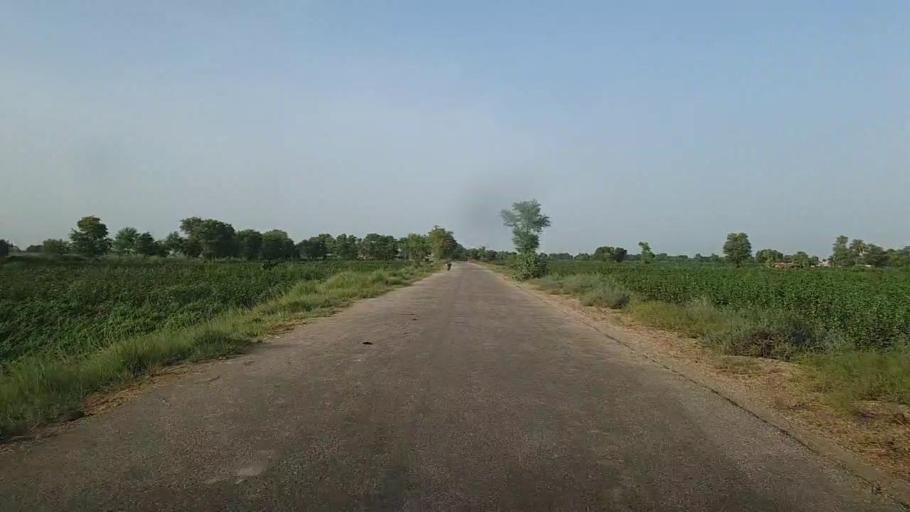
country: PK
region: Sindh
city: Ubauro
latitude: 28.1124
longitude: 69.8199
